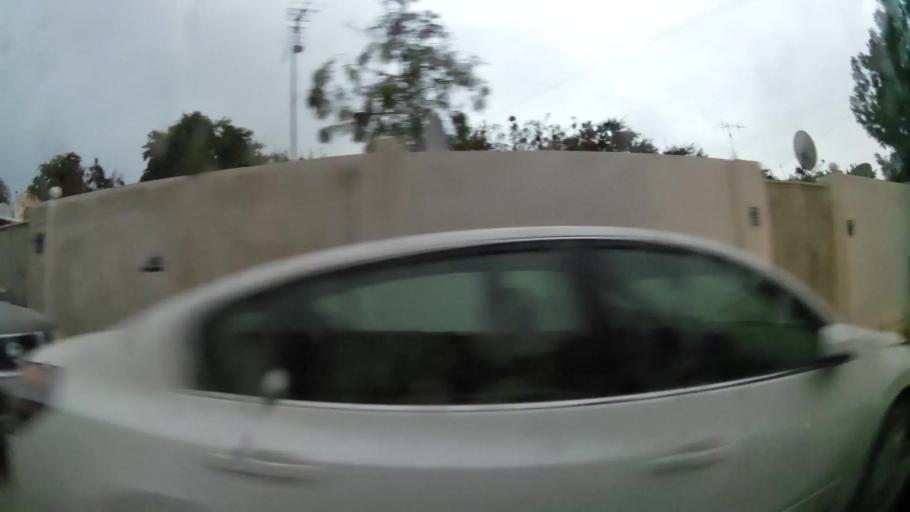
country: QA
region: Baladiyat ad Dawhah
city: Doha
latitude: 25.2694
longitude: 51.5172
